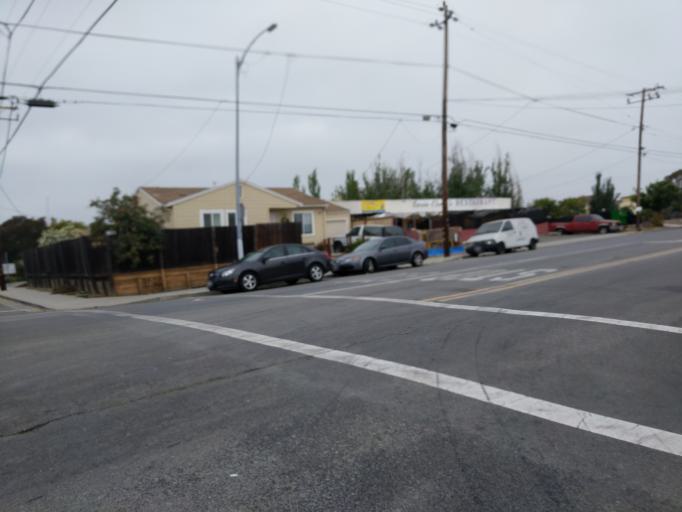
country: US
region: California
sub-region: Santa Clara County
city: Milpitas
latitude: 37.4262
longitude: -121.9760
